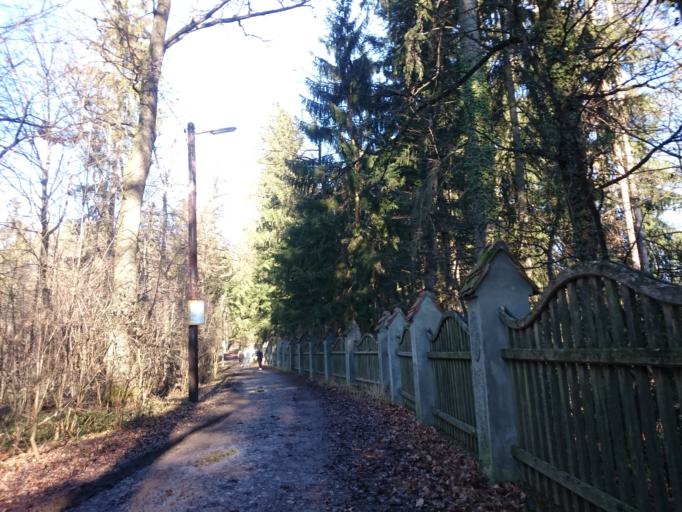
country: AT
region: Styria
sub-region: Graz Stadt
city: Graz
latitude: 47.0866
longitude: 15.4663
